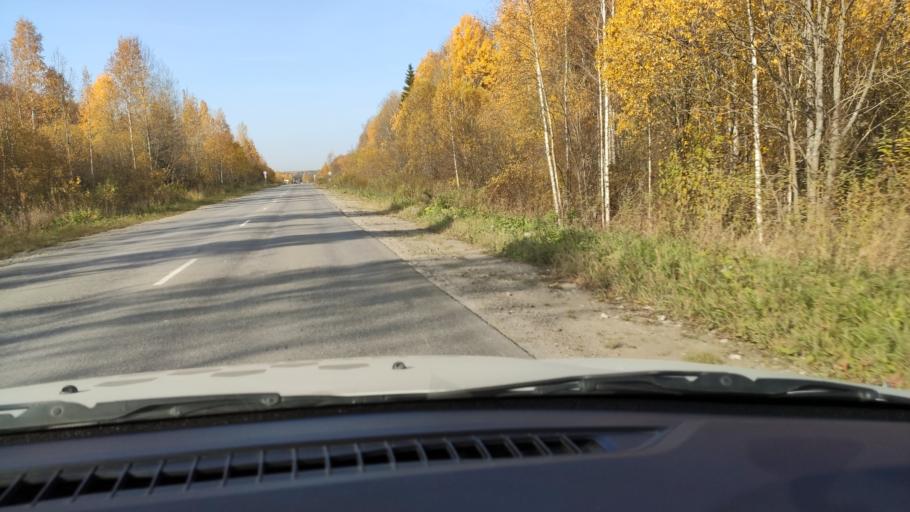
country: RU
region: Perm
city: Novyye Lyady
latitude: 58.0315
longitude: 56.6162
